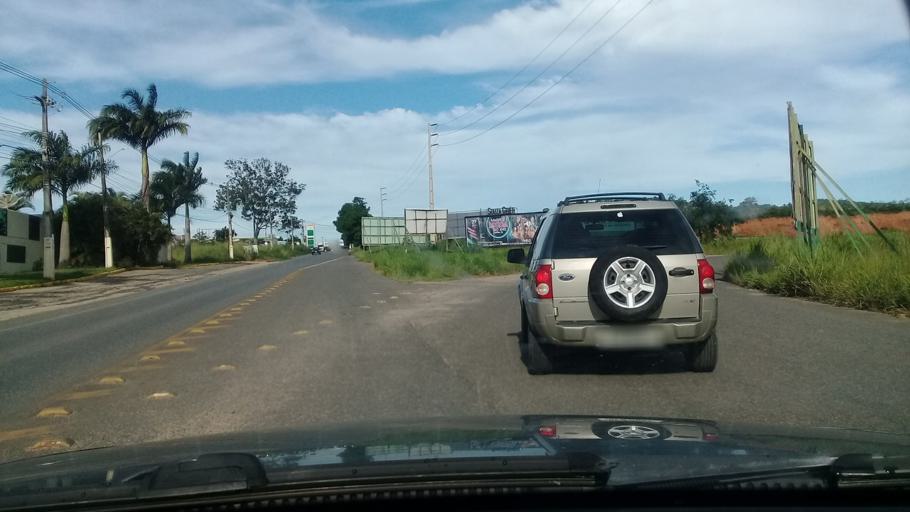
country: BR
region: Pernambuco
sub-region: Vitoria De Santo Antao
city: Vitoria de Santo Antao
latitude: -8.1162
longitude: -35.2675
